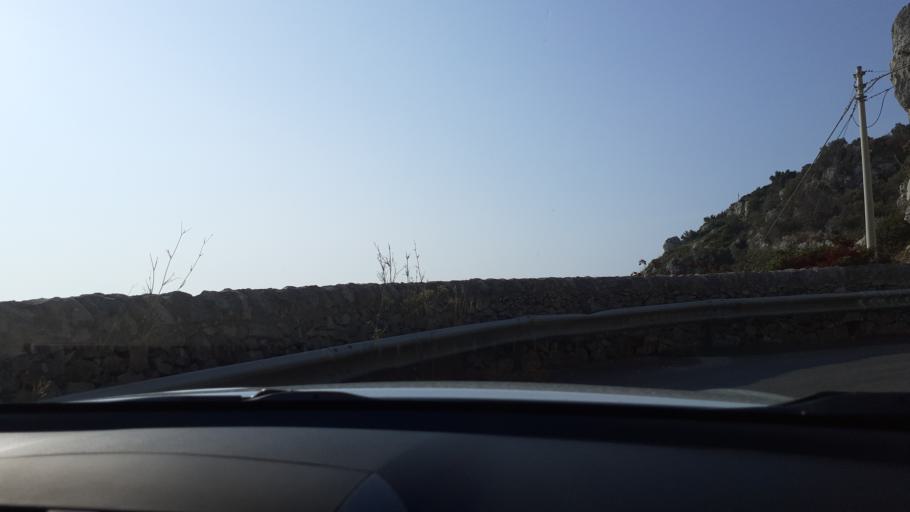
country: IT
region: Sicily
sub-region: Provincia di Siracusa
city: Cassibile
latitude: 36.9804
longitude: 15.1709
